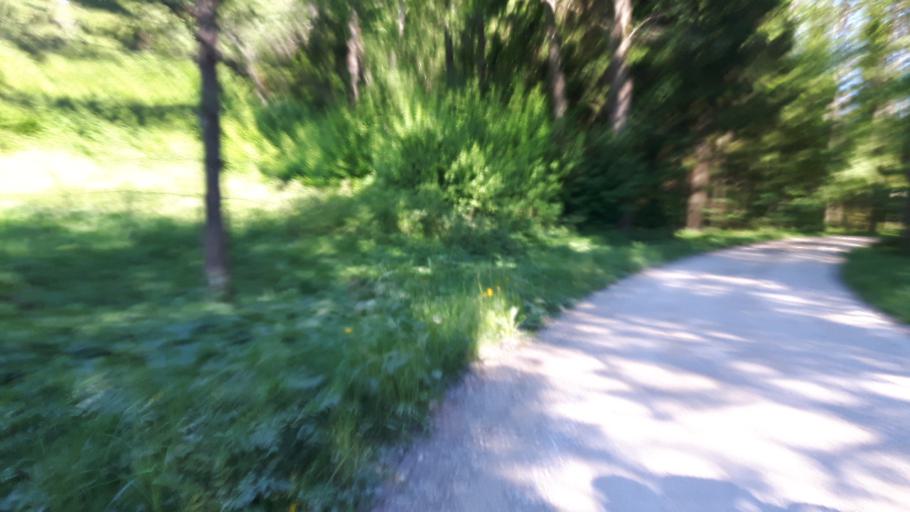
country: EE
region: Harju
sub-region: Loksa linn
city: Loksa
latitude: 59.5643
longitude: 25.8563
